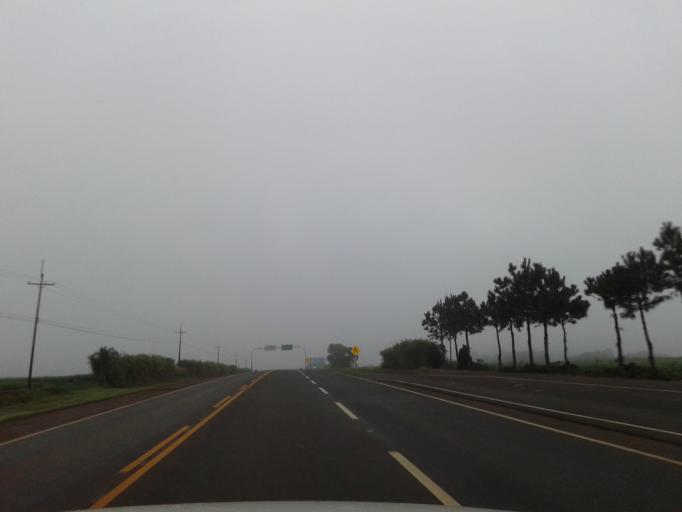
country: PY
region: Itapua
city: Pirapo
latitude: -26.9026
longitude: -55.4769
